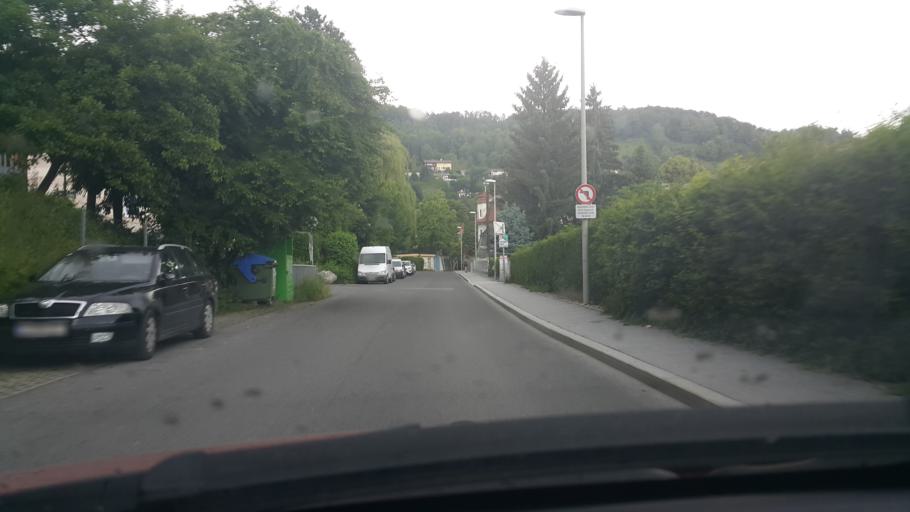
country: AT
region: Styria
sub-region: Graz Stadt
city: Wetzelsdorf
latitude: 47.0534
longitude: 15.3908
